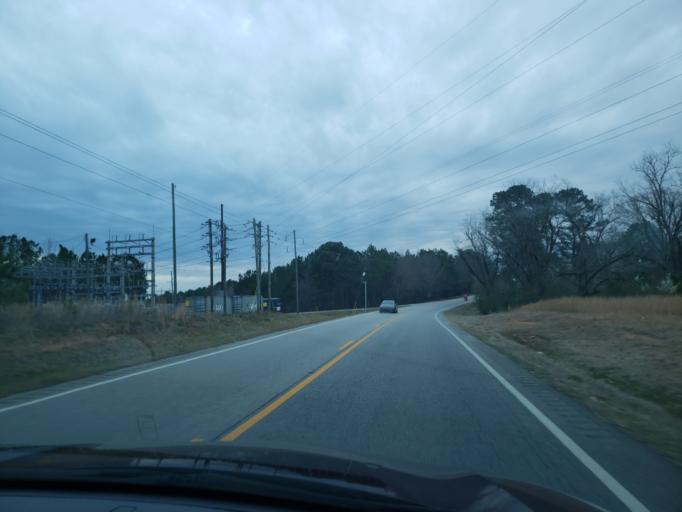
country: US
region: Alabama
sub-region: Chambers County
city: Lafayette
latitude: 33.0056
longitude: -85.3695
